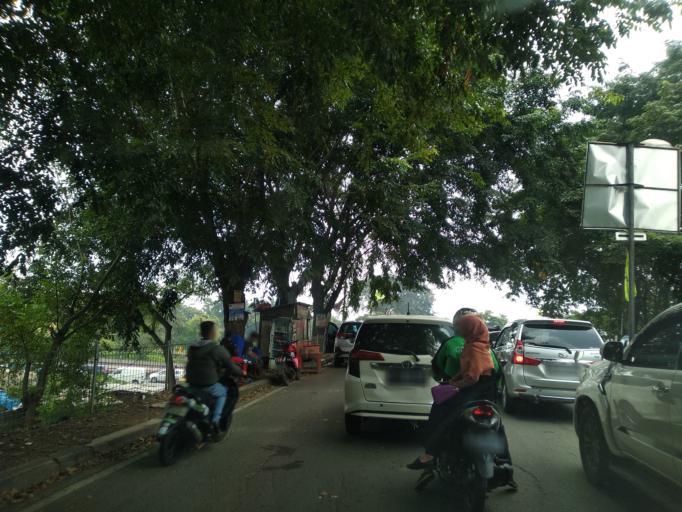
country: ID
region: West Java
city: Bekasi
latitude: -6.2738
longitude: 107.0454
